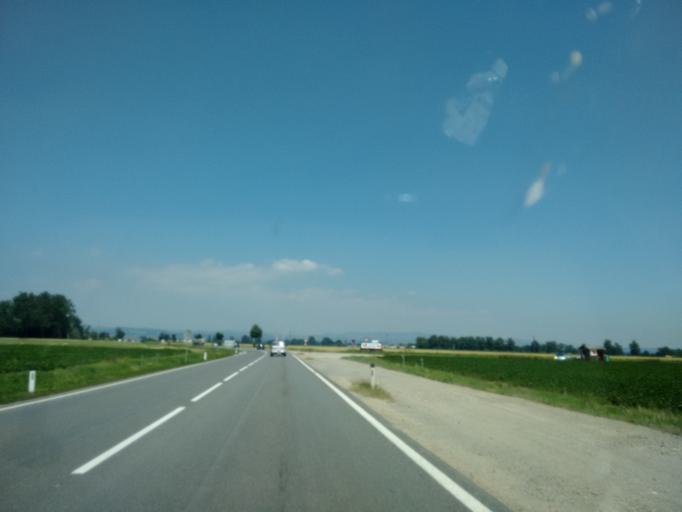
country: AT
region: Upper Austria
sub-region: Wels-Land
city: Buchkirchen
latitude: 48.2835
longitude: 14.0048
